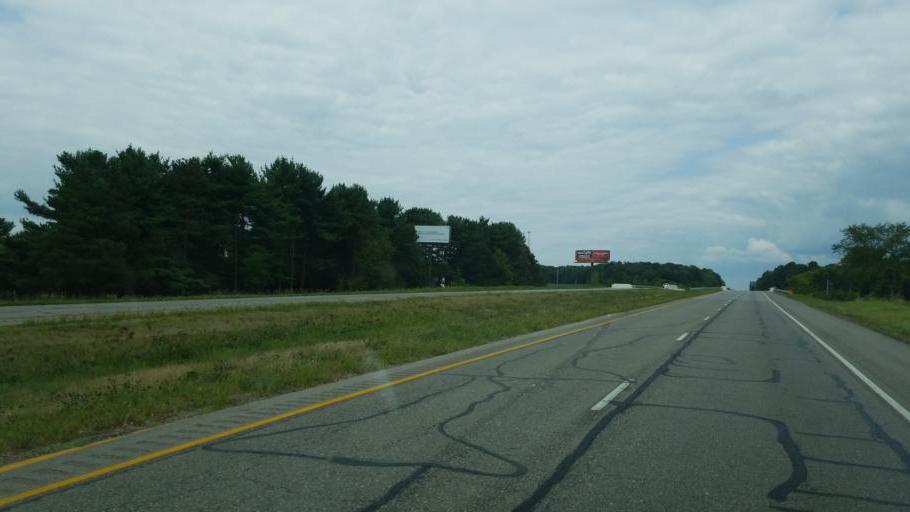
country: US
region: Ohio
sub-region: Columbiana County
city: Leetonia
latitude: 40.8260
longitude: -80.7424
